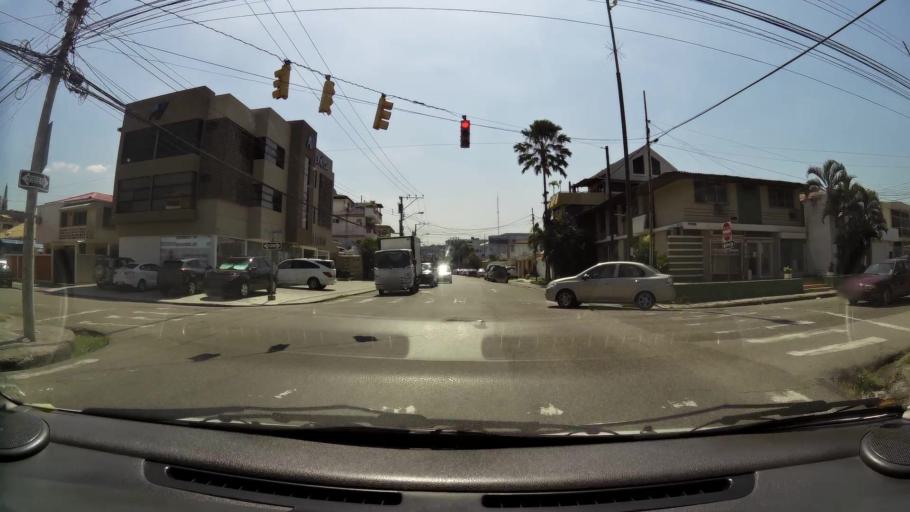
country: EC
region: Guayas
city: Guayaquil
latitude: -2.1667
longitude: -79.9131
